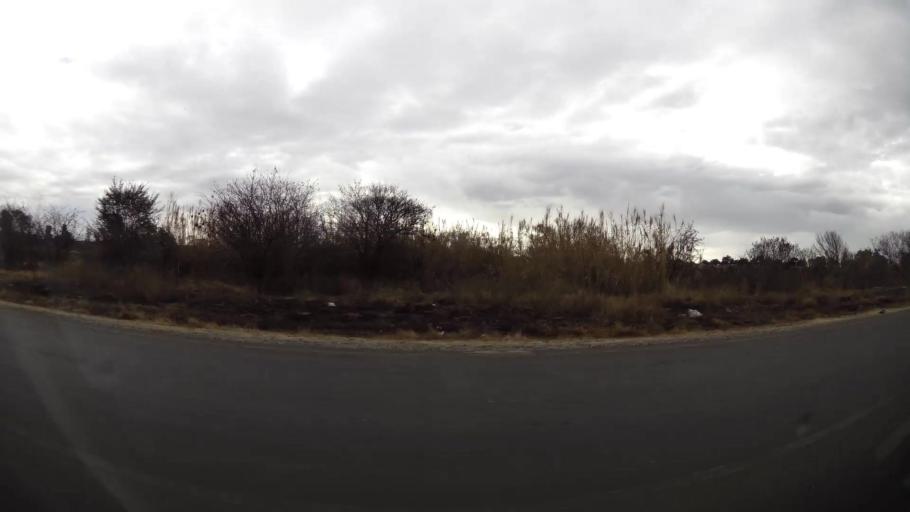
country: ZA
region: Orange Free State
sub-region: Fezile Dabi District Municipality
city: Kroonstad
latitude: -27.6503
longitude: 27.2271
